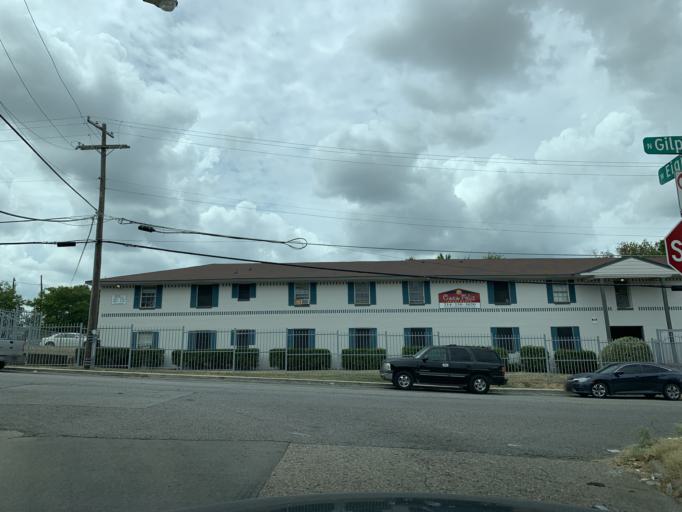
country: US
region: Texas
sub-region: Dallas County
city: Cockrell Hill
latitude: 32.7481
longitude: -96.8804
